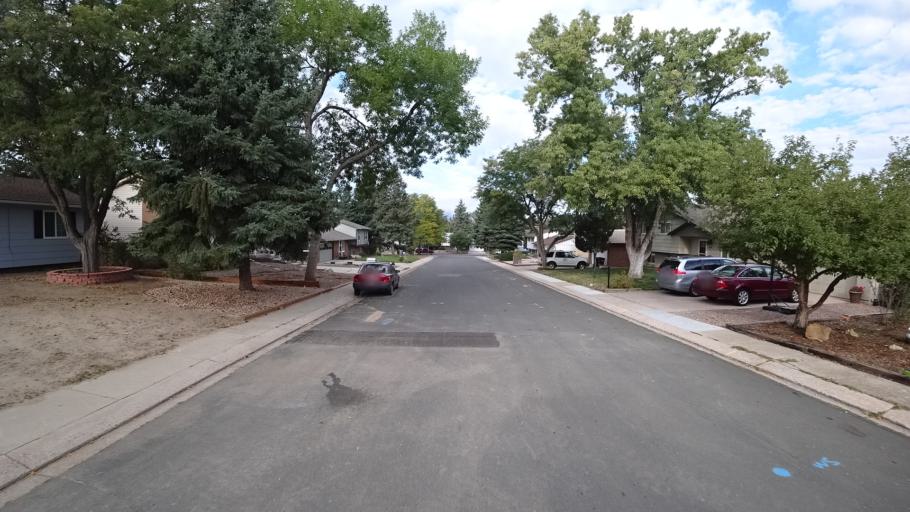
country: US
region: Colorado
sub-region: El Paso County
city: Cimarron Hills
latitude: 38.8656
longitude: -104.7527
